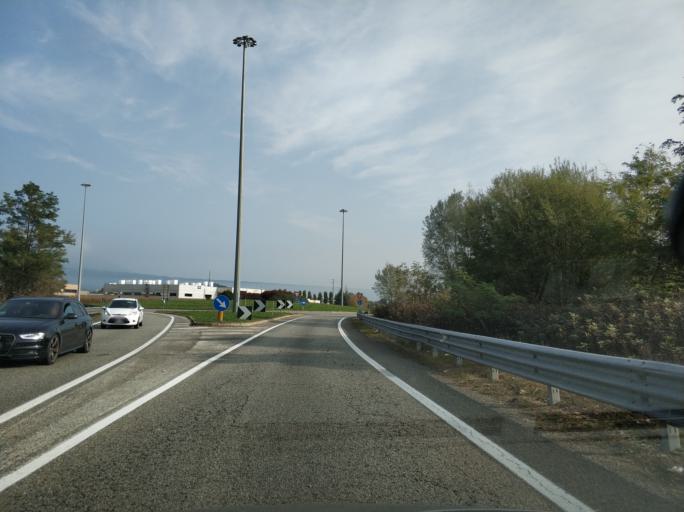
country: IT
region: Piedmont
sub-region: Provincia di Torino
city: Loranze
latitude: 45.4348
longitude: 7.8219
